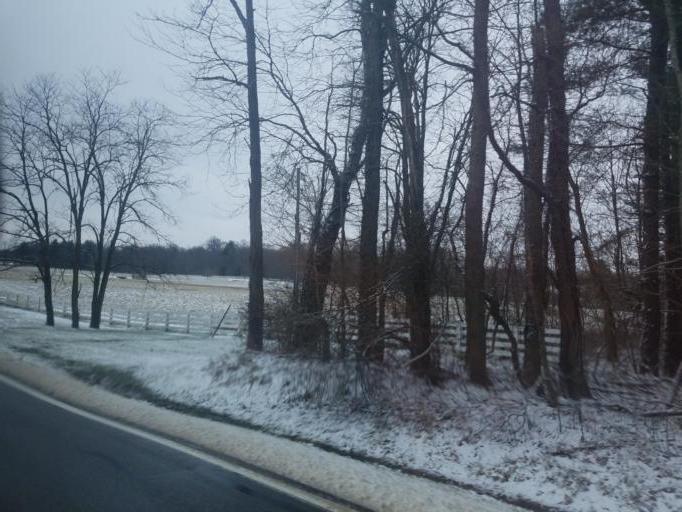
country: US
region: Ohio
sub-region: Franklin County
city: New Albany
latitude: 40.0722
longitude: -82.7918
